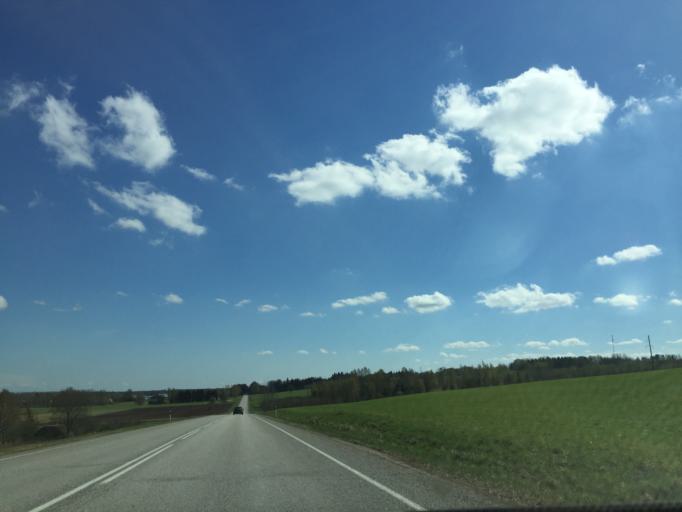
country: EE
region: Valgamaa
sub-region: Valga linn
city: Valga
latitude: 57.9010
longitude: 26.0498
